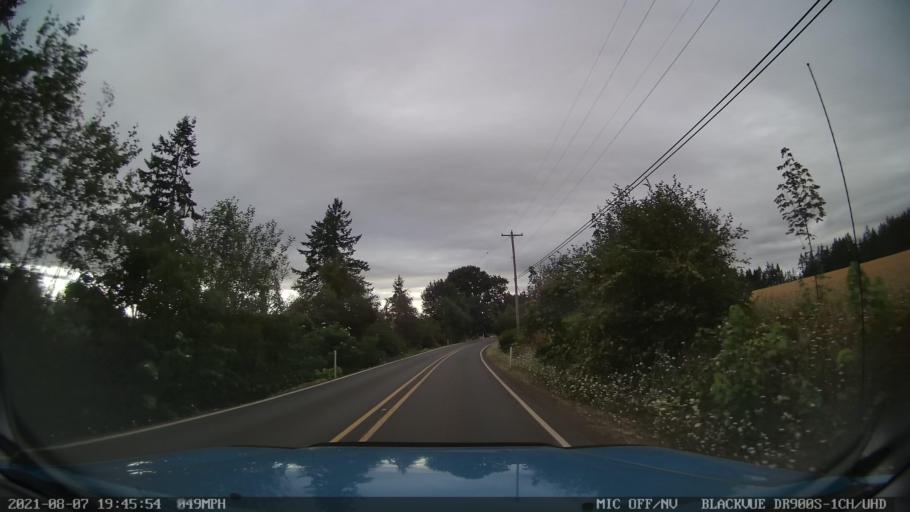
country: US
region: Oregon
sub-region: Marion County
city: Silverton
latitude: 44.9527
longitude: -122.6999
